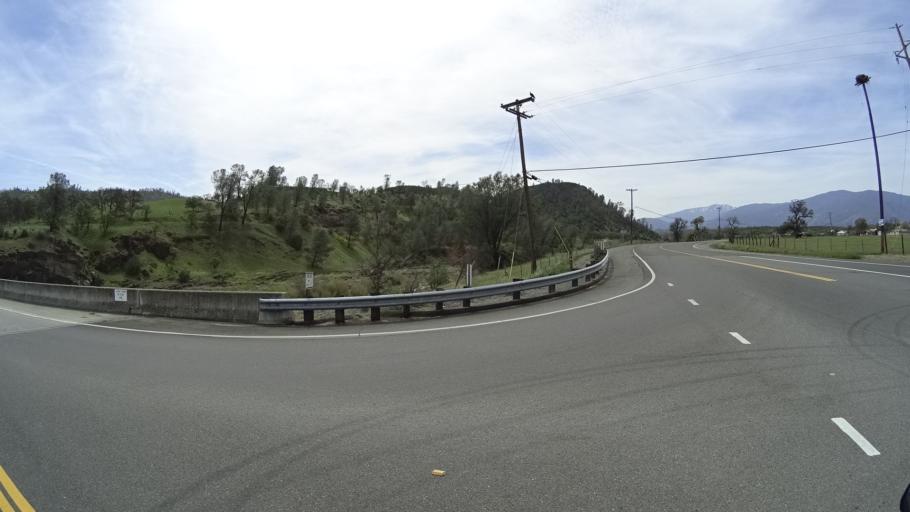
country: US
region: California
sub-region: Glenn County
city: Willows
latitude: 39.6118
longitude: -122.5303
